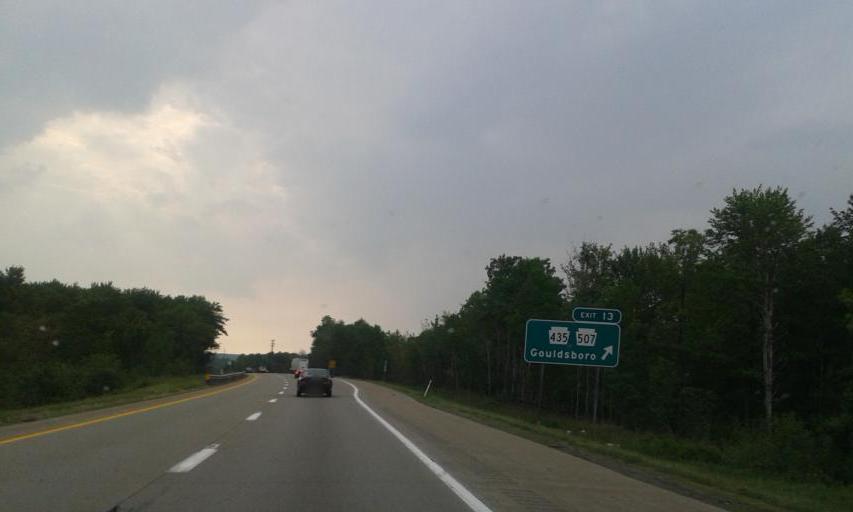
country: US
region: Pennsylvania
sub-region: Lackawanna County
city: Moscow
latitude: 41.2271
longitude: -75.4899
